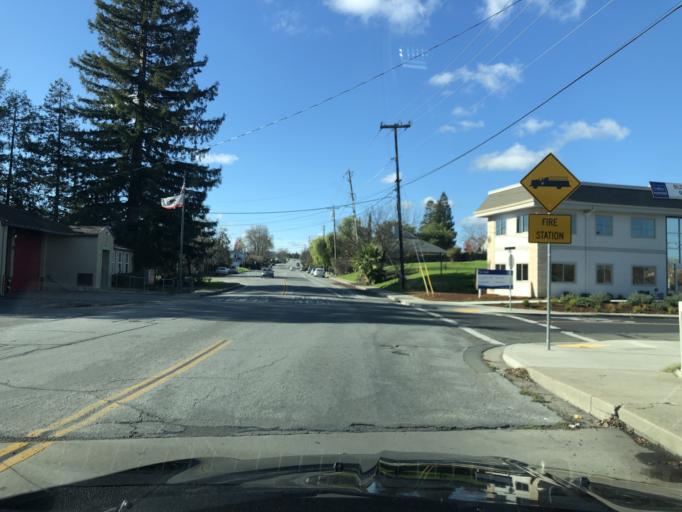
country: US
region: California
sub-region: Contra Costa County
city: Pacheco
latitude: 37.9834
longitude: -122.0688
